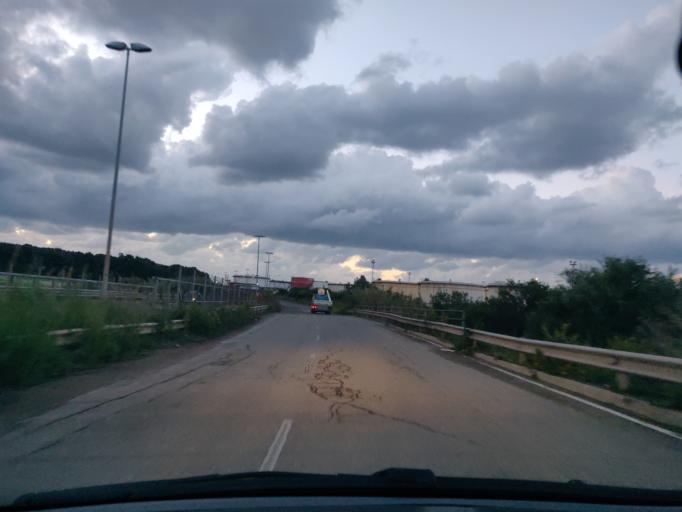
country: IT
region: Latium
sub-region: Citta metropolitana di Roma Capitale
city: Aurelia
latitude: 42.1146
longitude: 11.7794
